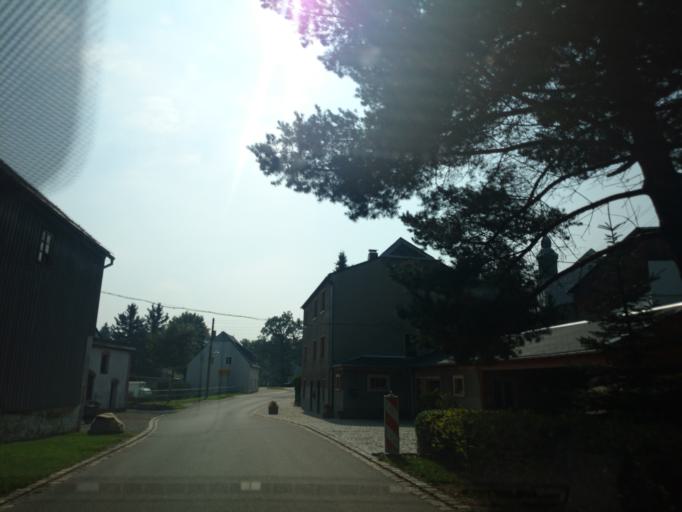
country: DE
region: Saxony
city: Eppendorf
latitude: 50.8295
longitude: 13.2171
